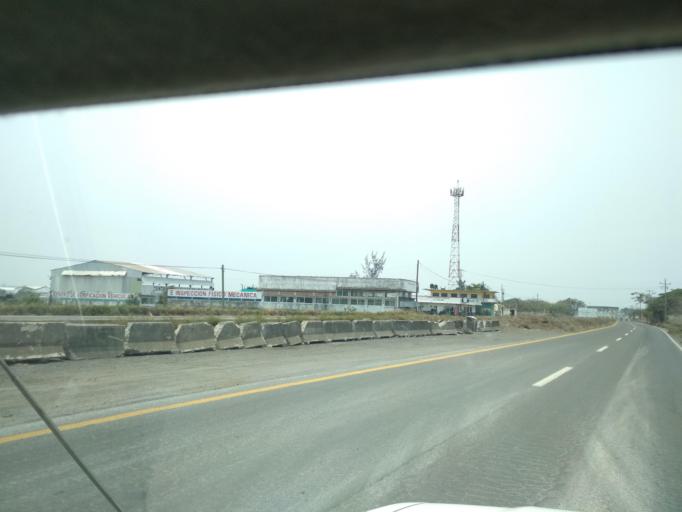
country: MX
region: Veracruz
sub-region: Veracruz
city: Delfino Victoria (Santa Fe)
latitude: 19.2064
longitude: -96.2646
